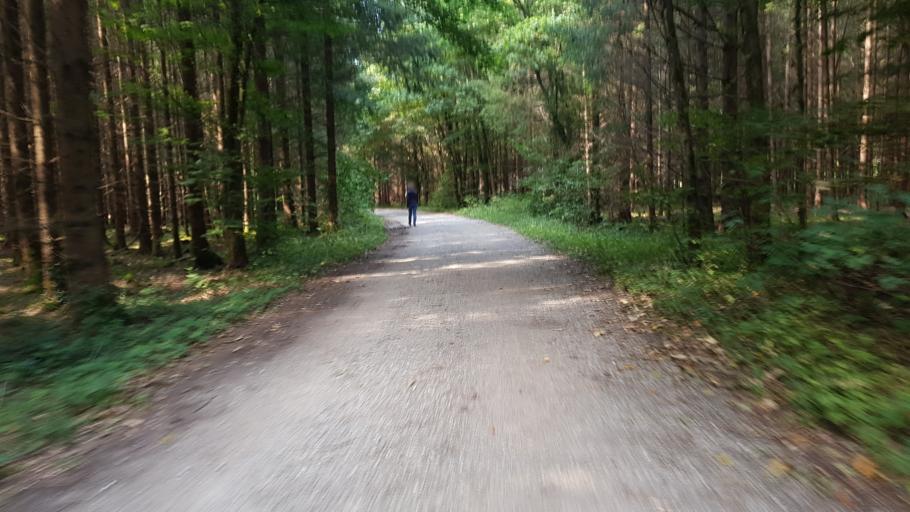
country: DE
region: Bavaria
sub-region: Upper Bavaria
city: Wessling
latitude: 48.0684
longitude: 11.2287
